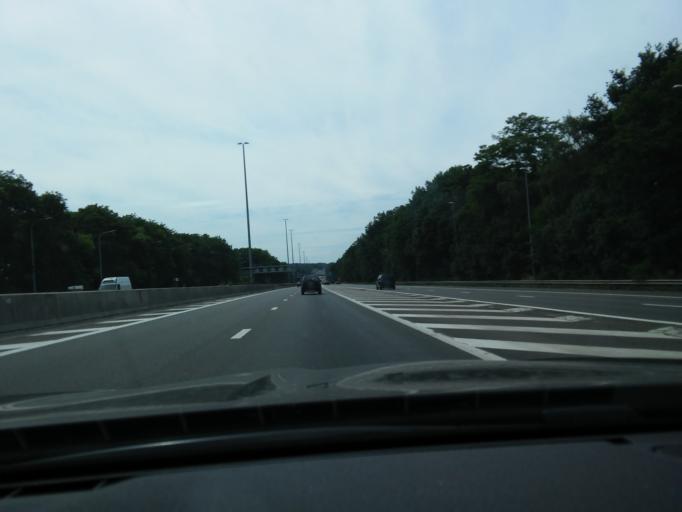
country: BE
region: Flanders
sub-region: Provincie Vlaams-Brabant
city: Bertem
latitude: 50.8583
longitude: 4.6326
